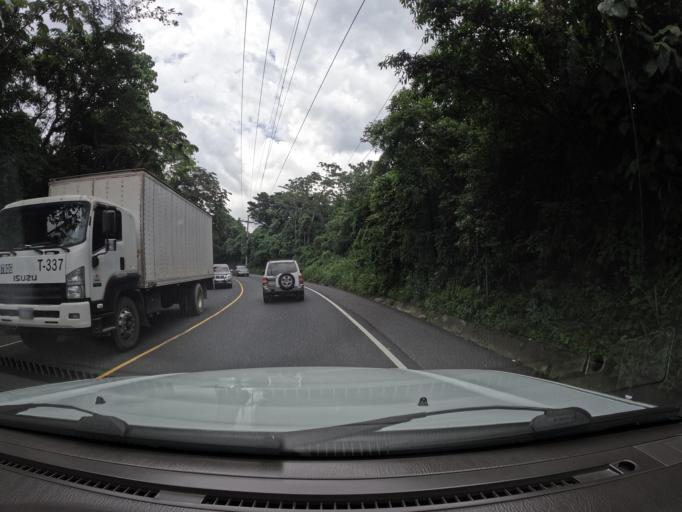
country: GT
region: Sacatepequez
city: Alotenango
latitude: 14.4246
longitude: -90.8201
